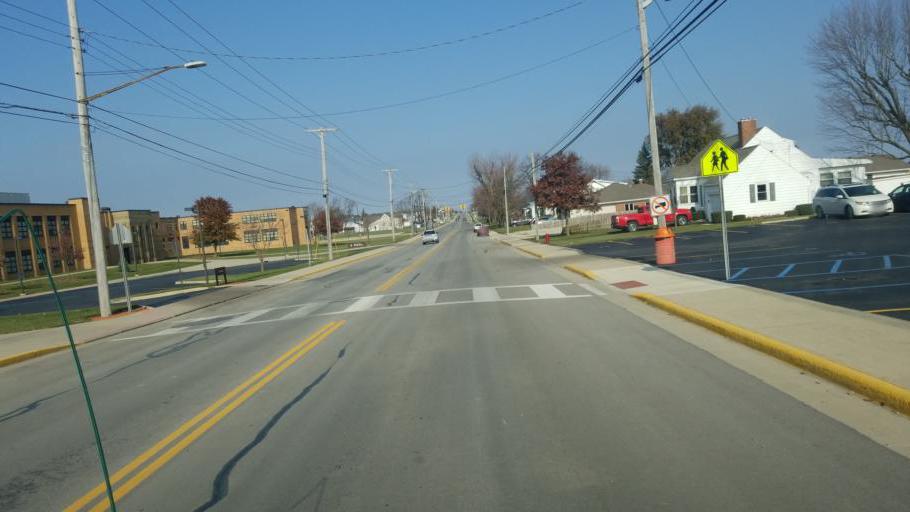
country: US
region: Ohio
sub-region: Mercer County
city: Coldwater
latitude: 40.4818
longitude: -84.6287
